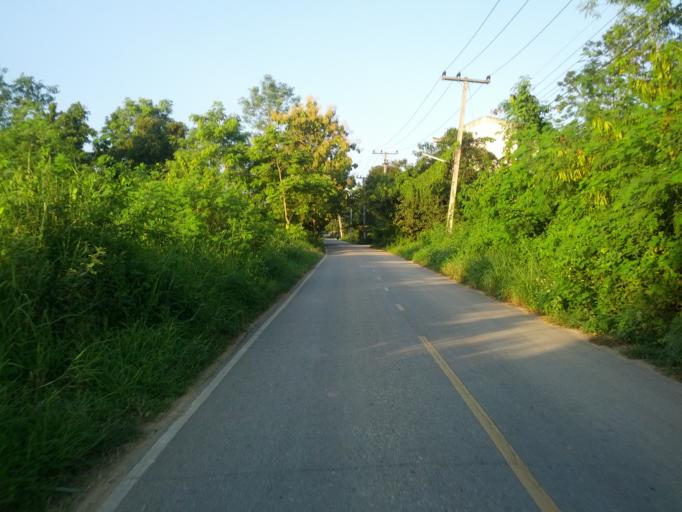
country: TH
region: Chiang Mai
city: San Kamphaeng
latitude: 18.7644
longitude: 99.0981
